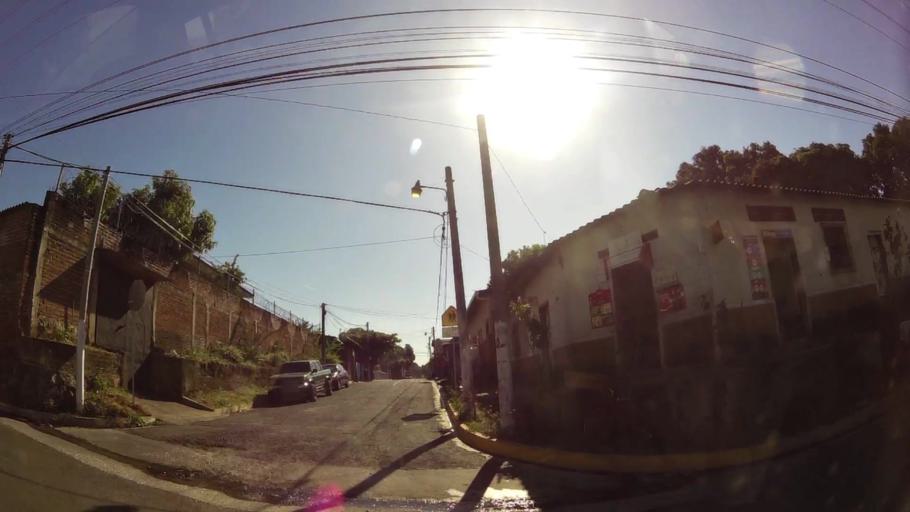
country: SV
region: Sonsonate
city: Sonzacate
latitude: 13.7367
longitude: -89.7169
